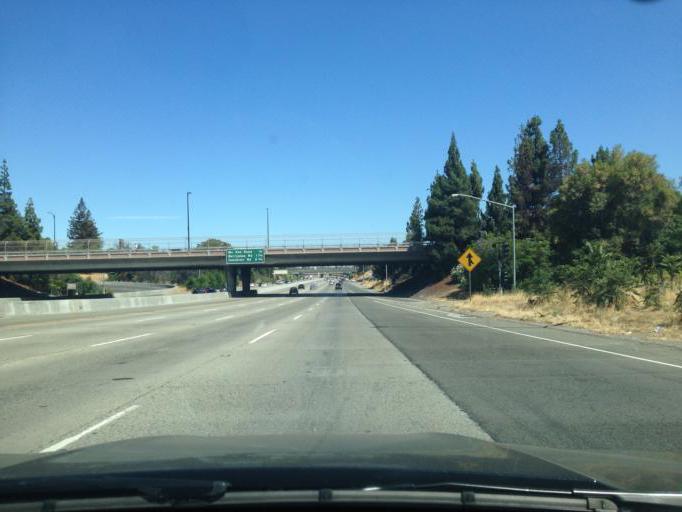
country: US
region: California
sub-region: Santa Clara County
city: Alum Rock
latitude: 37.3587
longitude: -121.8403
